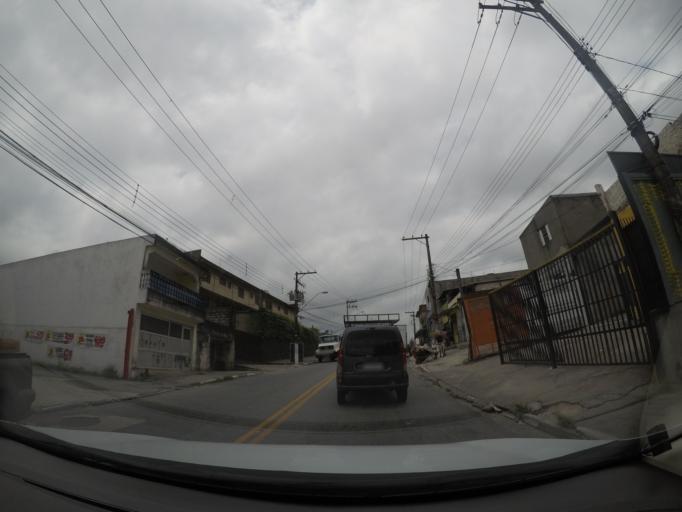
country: BR
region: Sao Paulo
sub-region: Itaquaquecetuba
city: Itaquaquecetuba
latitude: -23.4569
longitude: -46.4096
